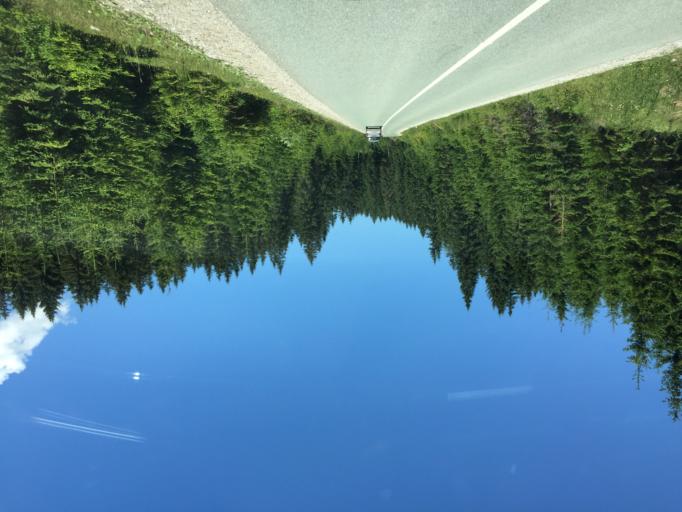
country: SI
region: Bohinj
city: Bohinjska Bistrica
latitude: 46.3417
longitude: 13.9621
